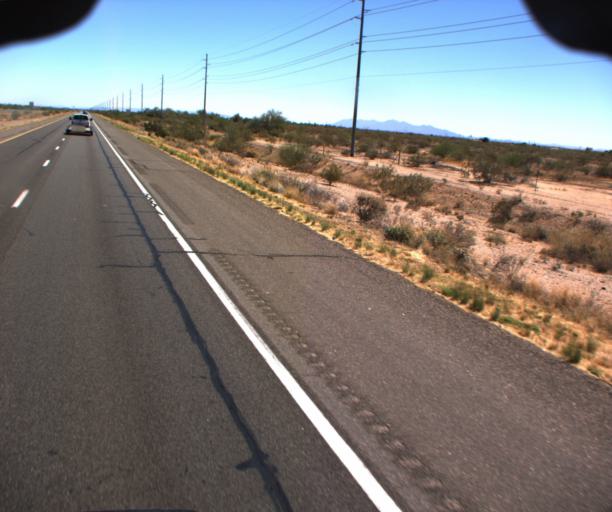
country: US
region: Arizona
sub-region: Maricopa County
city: Sun City West
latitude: 33.7327
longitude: -112.4709
